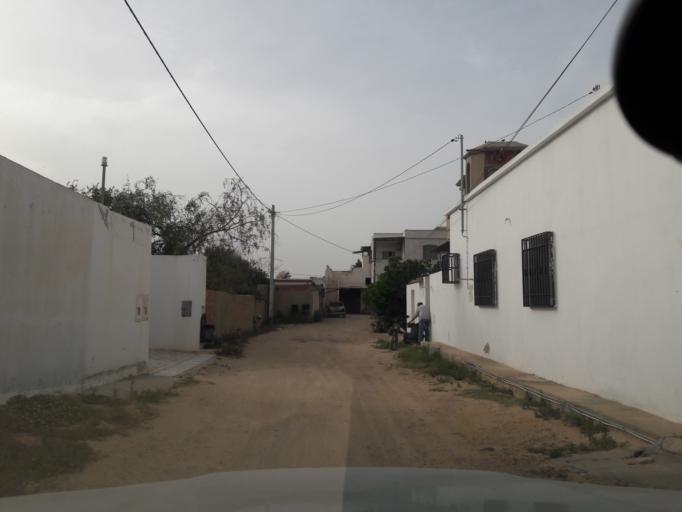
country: TN
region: Safaqis
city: Al Qarmadah
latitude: 34.7809
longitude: 10.7681
